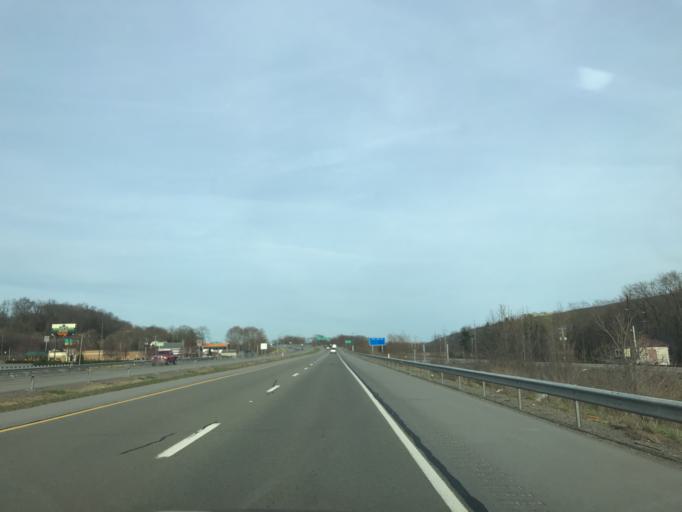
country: US
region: Pennsylvania
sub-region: Lycoming County
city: Kenmar
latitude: 41.2458
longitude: -76.9580
